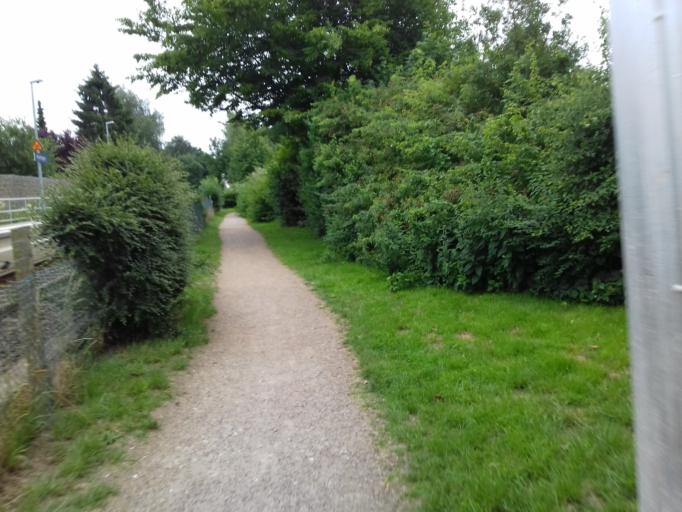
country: DE
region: Schleswig-Holstein
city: Kronshagen
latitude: 54.3308
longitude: 10.0834
